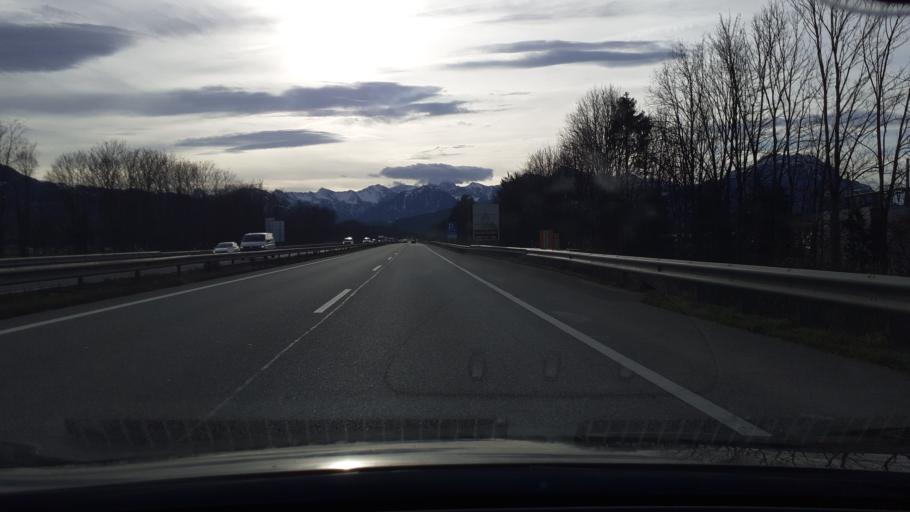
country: AT
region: Vorarlberg
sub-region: Politischer Bezirk Feldkirch
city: Klaus
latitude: 47.3052
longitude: 9.6224
